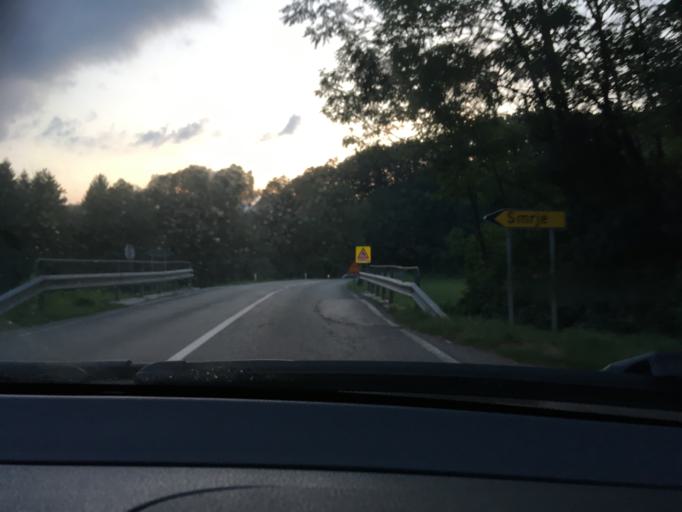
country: SI
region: Pivka
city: Pivka
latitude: 45.6007
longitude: 14.2005
